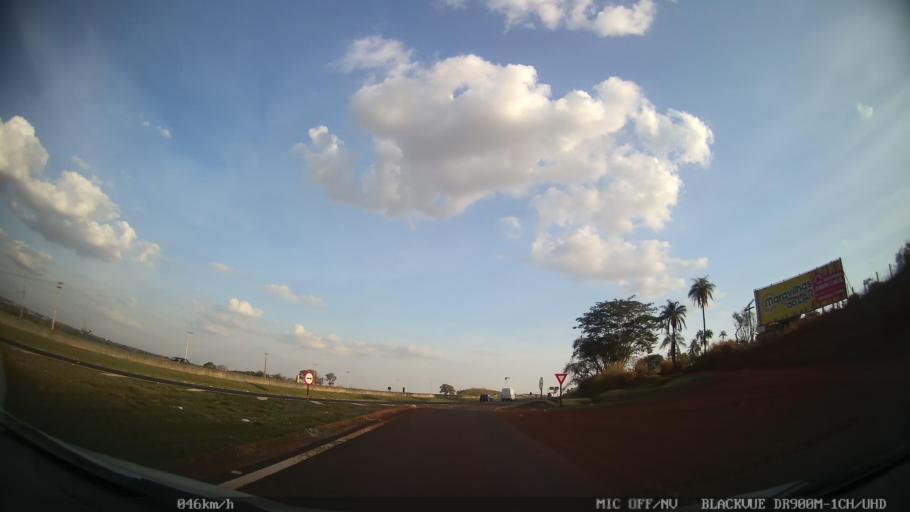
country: BR
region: Sao Paulo
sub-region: Jardinopolis
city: Jardinopolis
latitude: -21.1027
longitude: -47.7670
